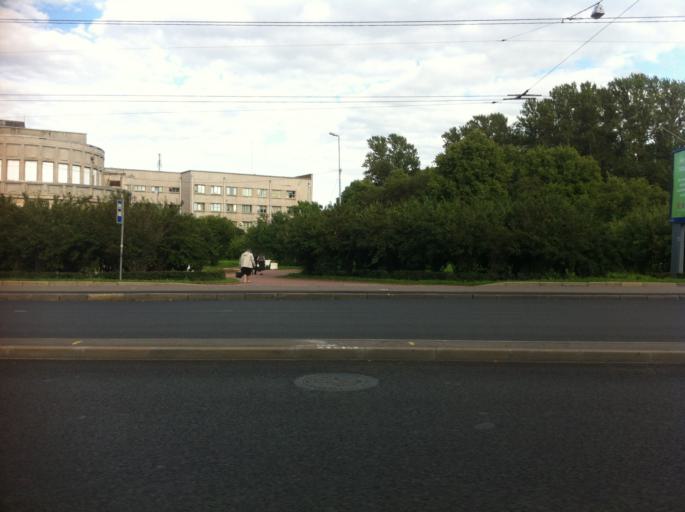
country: RU
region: St.-Petersburg
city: Admiralteisky
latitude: 59.8939
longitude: 30.2749
